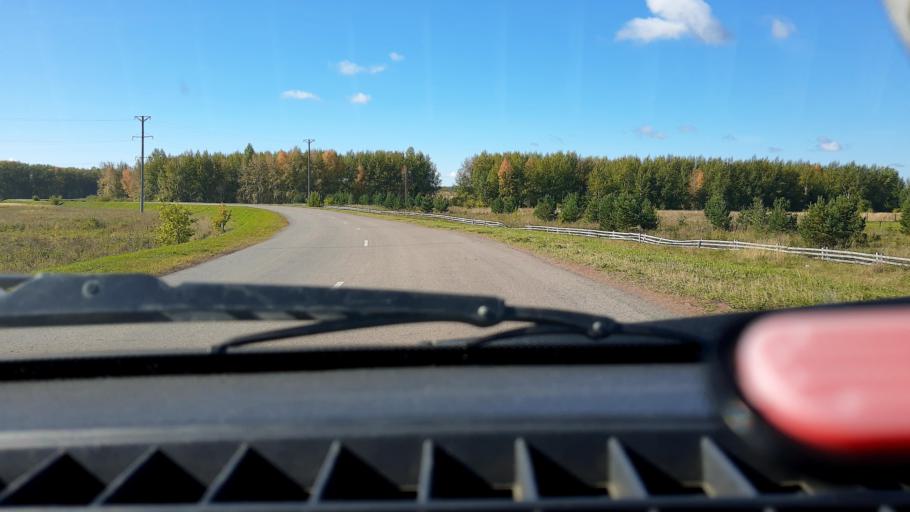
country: RU
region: Bashkortostan
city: Kushnarenkovo
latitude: 55.0883
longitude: 55.4799
